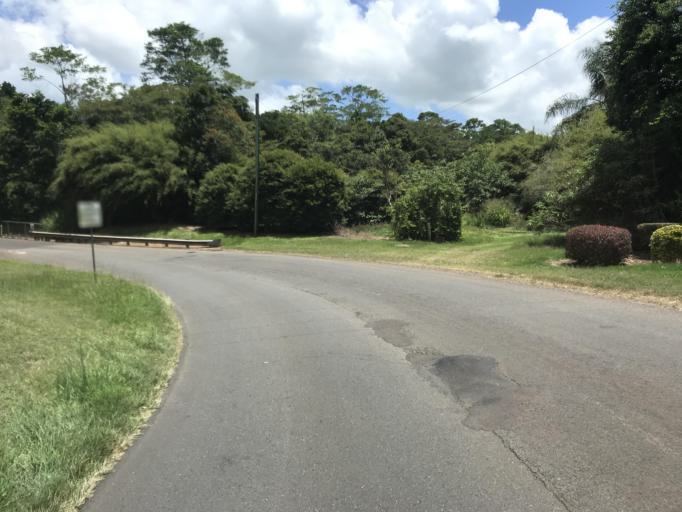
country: AU
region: Queensland
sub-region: Tablelands
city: Atherton
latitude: -17.3476
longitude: 145.5964
